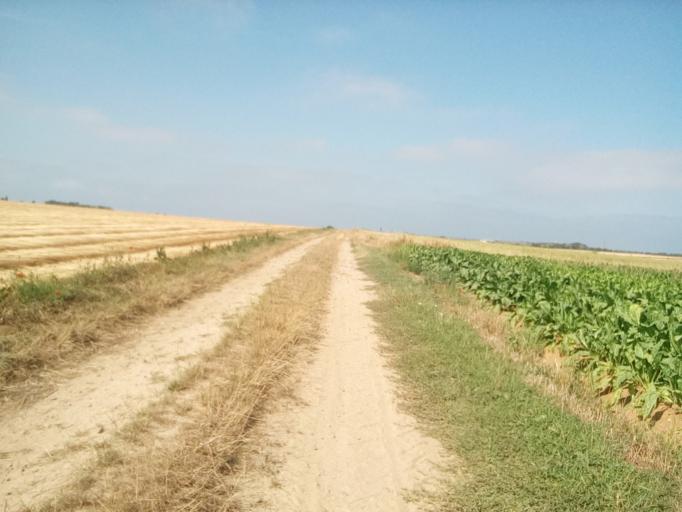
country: FR
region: Lower Normandy
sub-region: Departement du Calvados
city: Bernieres-sur-Mer
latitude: 49.3130
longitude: -0.4394
